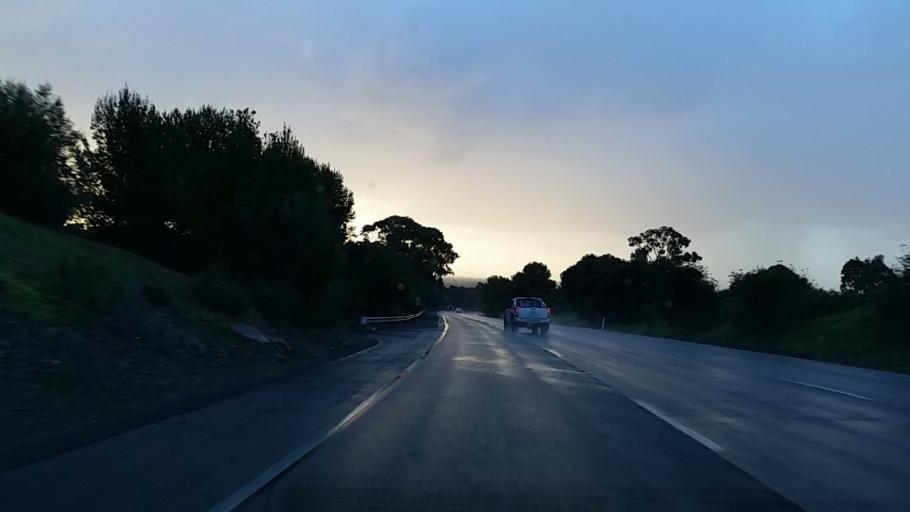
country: AU
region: South Australia
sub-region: Onkaparinga
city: Bedford Park
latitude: -35.0422
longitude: 138.5604
